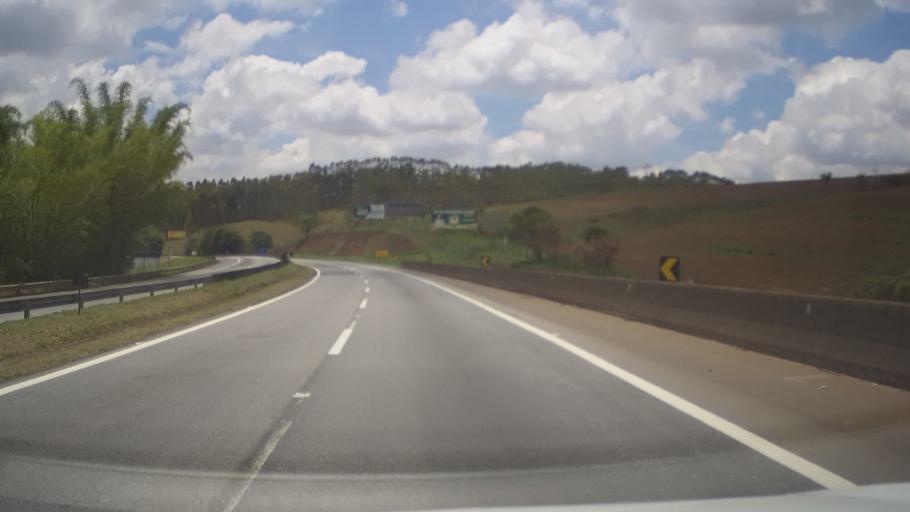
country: BR
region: Minas Gerais
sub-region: Tres Coracoes
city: Tres Coracoes
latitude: -21.6945
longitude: -45.3548
